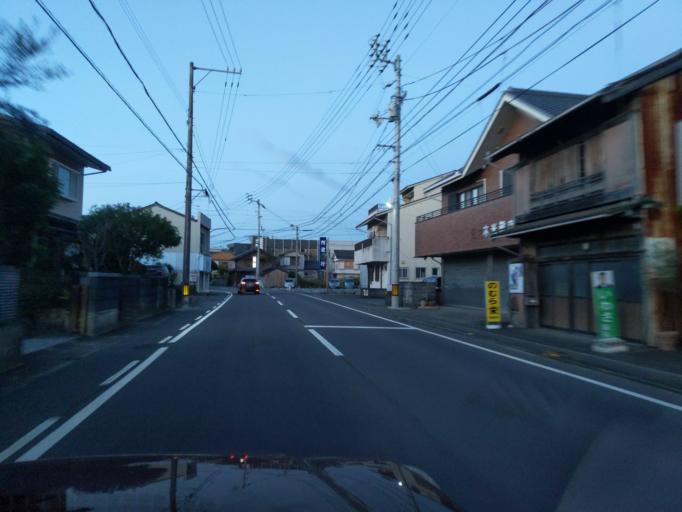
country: JP
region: Tokushima
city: Anan
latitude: 33.8753
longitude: 134.6445
